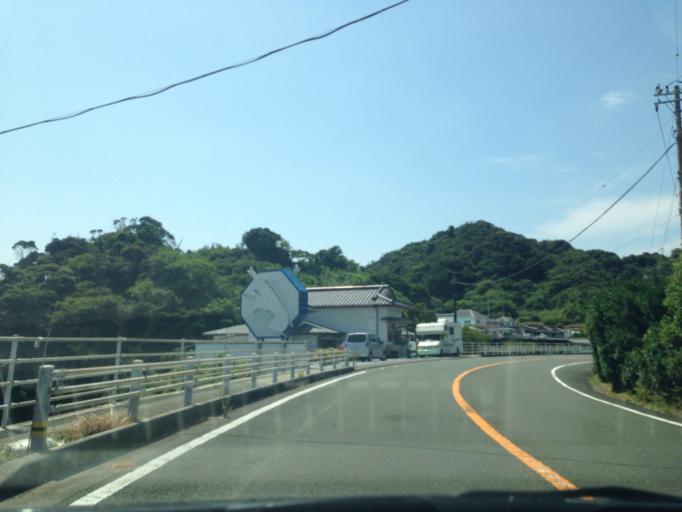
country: JP
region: Shizuoka
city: Shimoda
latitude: 34.6140
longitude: 138.8562
